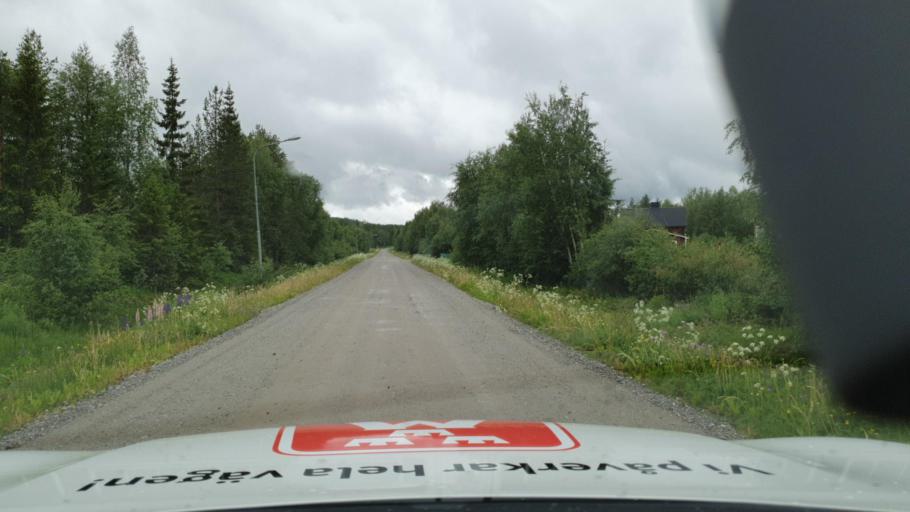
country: SE
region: Vaesterbotten
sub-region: Dorotea Kommun
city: Dorotea
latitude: 64.0919
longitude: 16.6647
